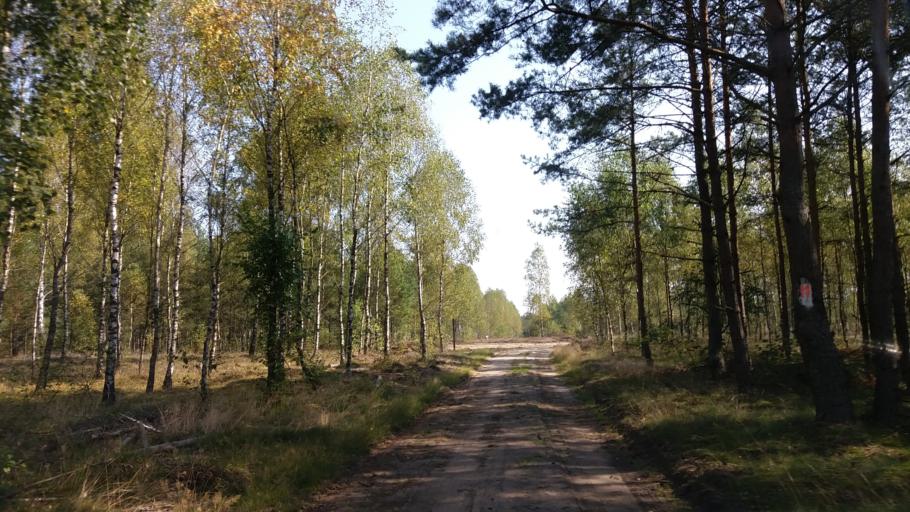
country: PL
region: West Pomeranian Voivodeship
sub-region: Powiat drawski
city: Kalisz Pomorski
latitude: 53.1368
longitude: 15.9412
